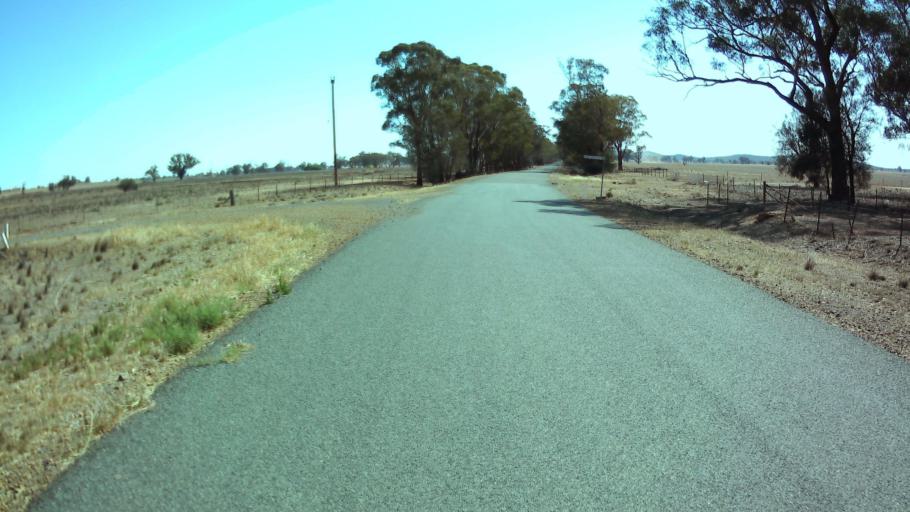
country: AU
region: New South Wales
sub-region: Weddin
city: Grenfell
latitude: -33.7286
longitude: 147.8907
